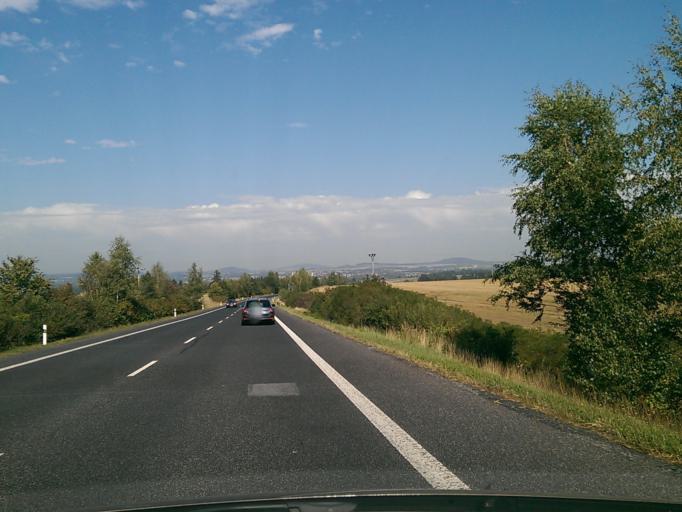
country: CZ
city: Hradek nad Nisou
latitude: 50.8591
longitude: 14.8575
